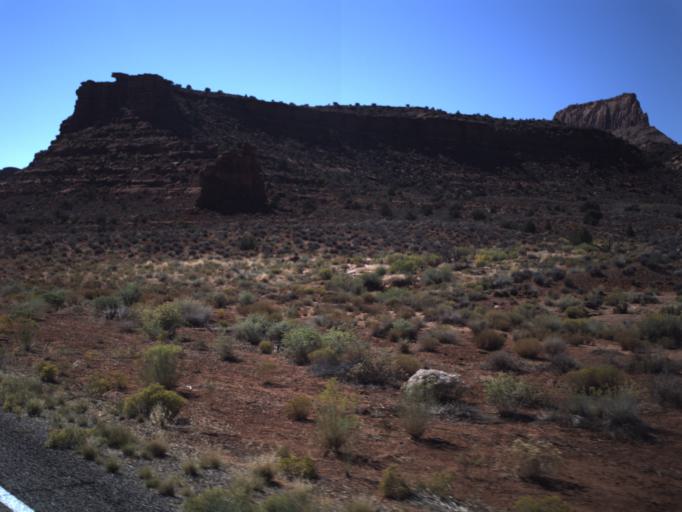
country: US
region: Utah
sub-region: San Juan County
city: Blanding
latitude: 37.7811
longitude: -110.2922
